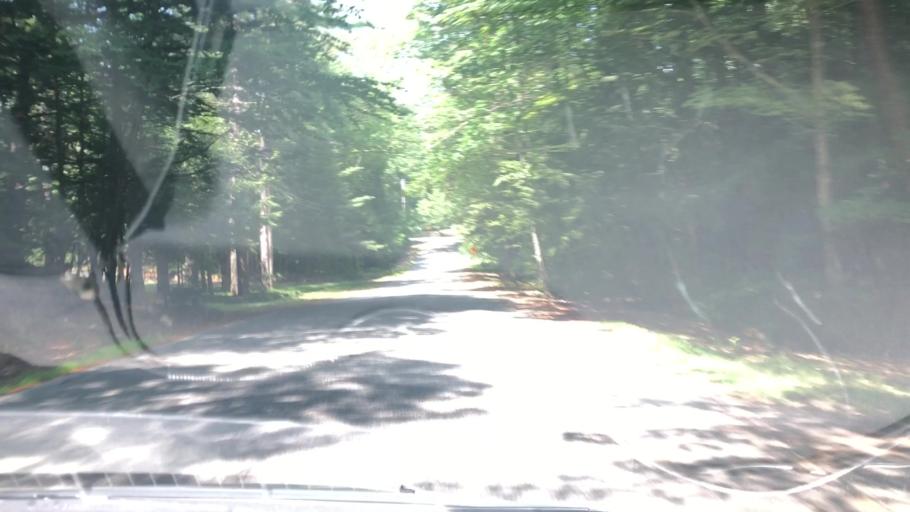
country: US
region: New Hampshire
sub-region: Hillsborough County
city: Milford
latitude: 42.8758
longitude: -71.6328
